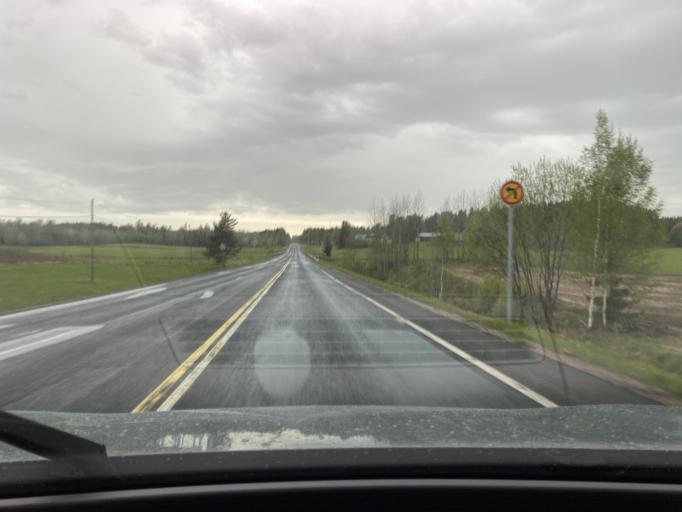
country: FI
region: Varsinais-Suomi
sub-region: Salo
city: Suomusjaervi
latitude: 60.3740
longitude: 23.6232
